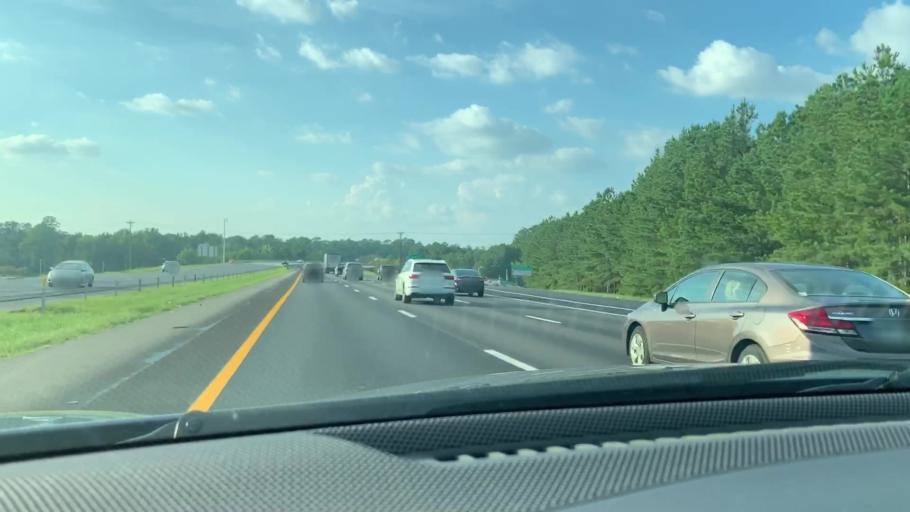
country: US
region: South Carolina
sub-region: Richland County
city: Forest Acres
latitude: 33.9930
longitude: -80.9563
